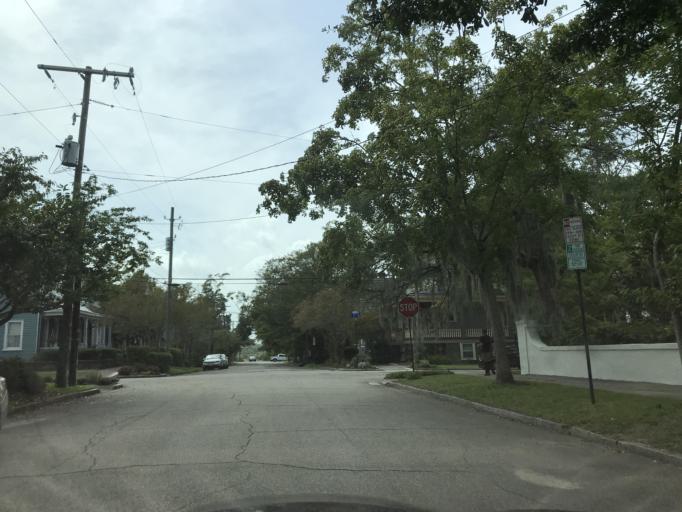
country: US
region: North Carolina
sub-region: New Hanover County
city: Wilmington
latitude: 34.2305
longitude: -77.9465
